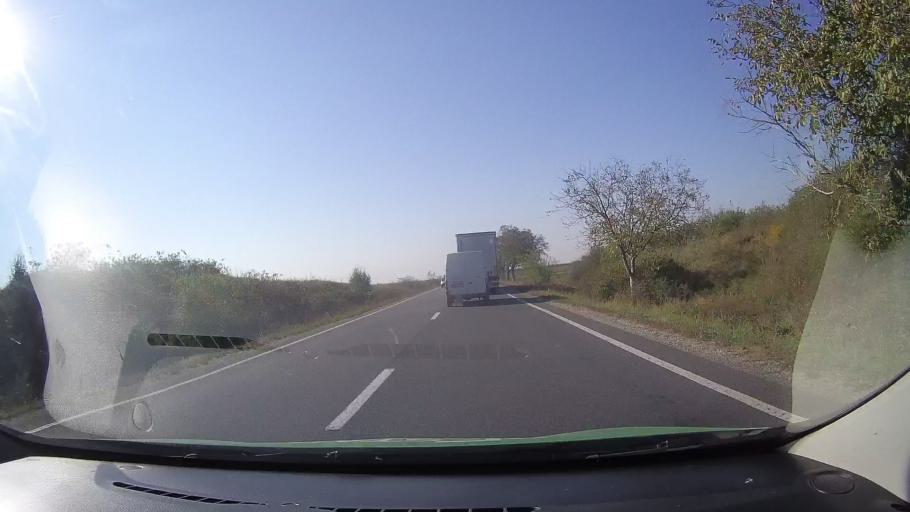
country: RO
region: Satu Mare
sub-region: Comuna Petresti
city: Petresti
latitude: 47.6354
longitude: 22.3989
